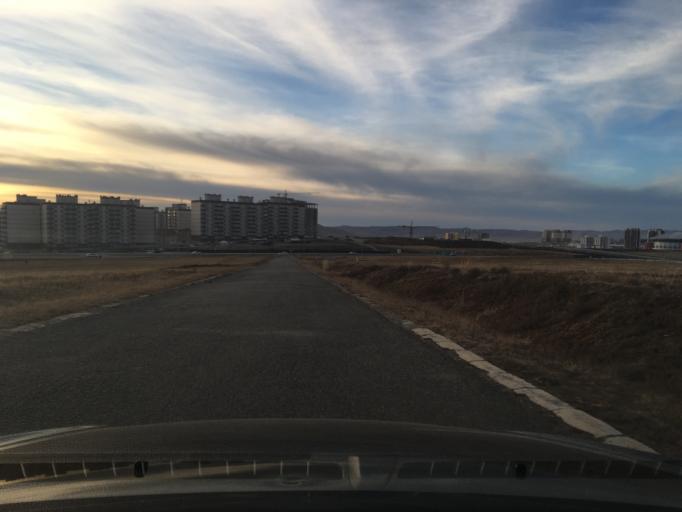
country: MN
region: Ulaanbaatar
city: Ulaanbaatar
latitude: 47.8451
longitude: 106.7944
